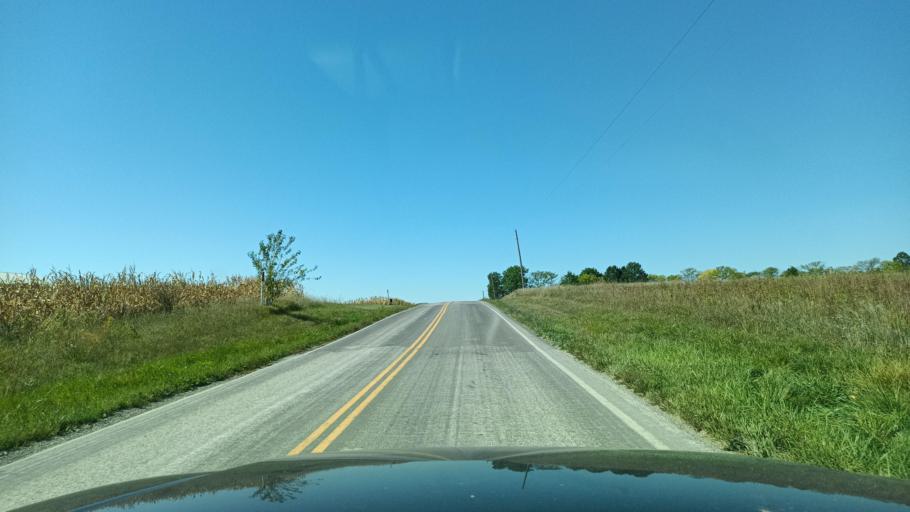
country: US
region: Missouri
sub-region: Macon County
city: La Plata
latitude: 40.0229
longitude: -92.5775
